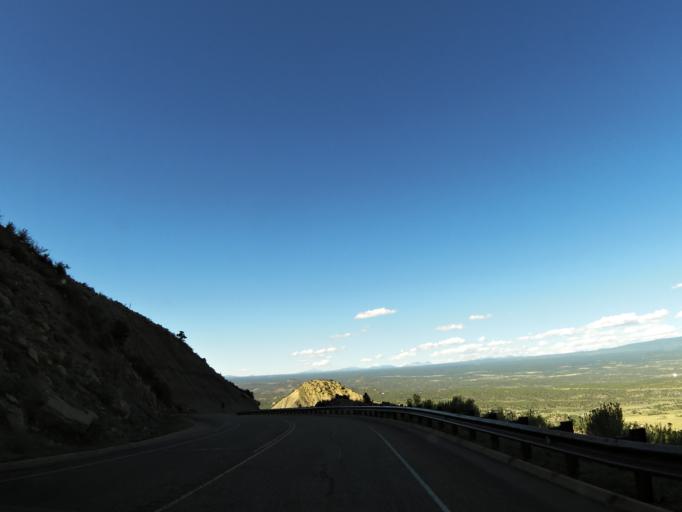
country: US
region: Colorado
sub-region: Montezuma County
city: Mancos
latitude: 37.3148
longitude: -108.4151
